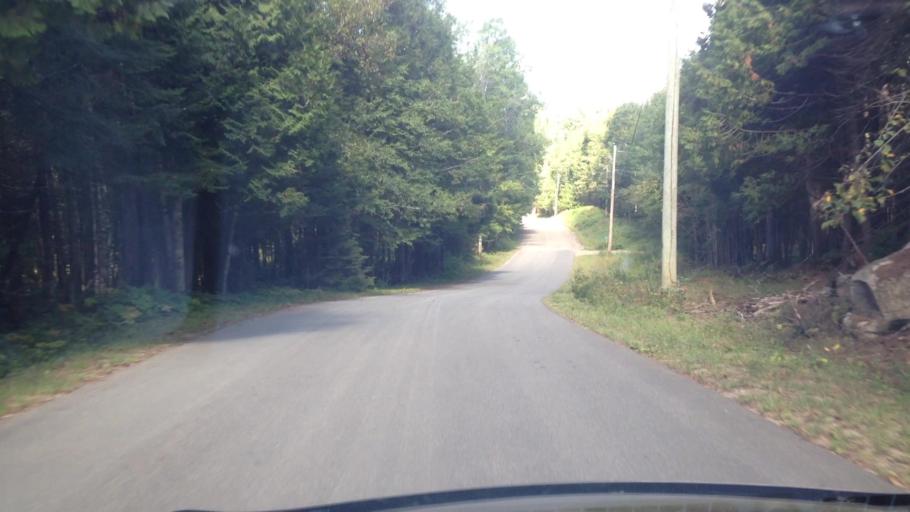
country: CA
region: Quebec
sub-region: Laurentides
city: Mont-Tremblant
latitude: 45.9431
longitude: -74.5885
